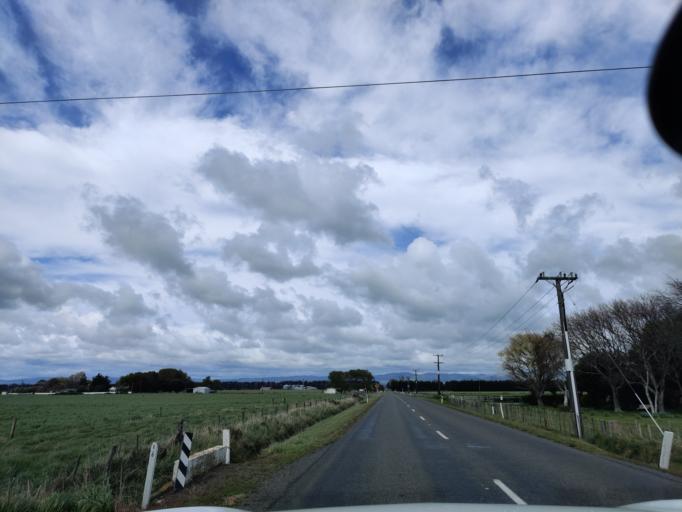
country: NZ
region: Manawatu-Wanganui
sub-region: Palmerston North City
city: Palmerston North
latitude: -40.3323
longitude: 175.5134
